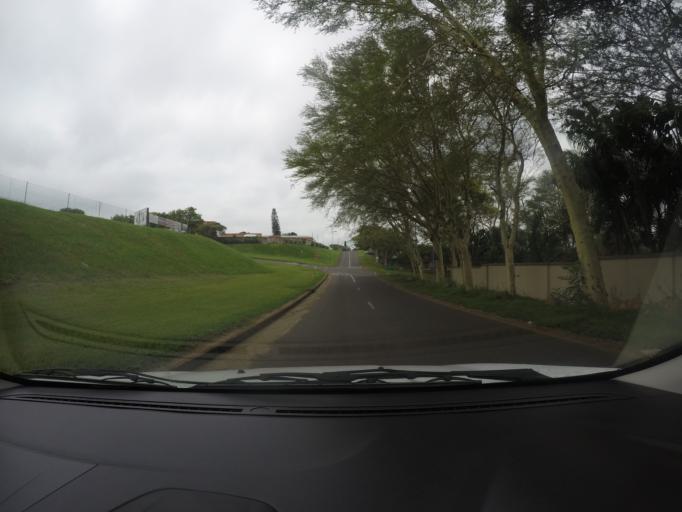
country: ZA
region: KwaZulu-Natal
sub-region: uThungulu District Municipality
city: Empangeni
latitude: -28.7524
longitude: 31.8864
